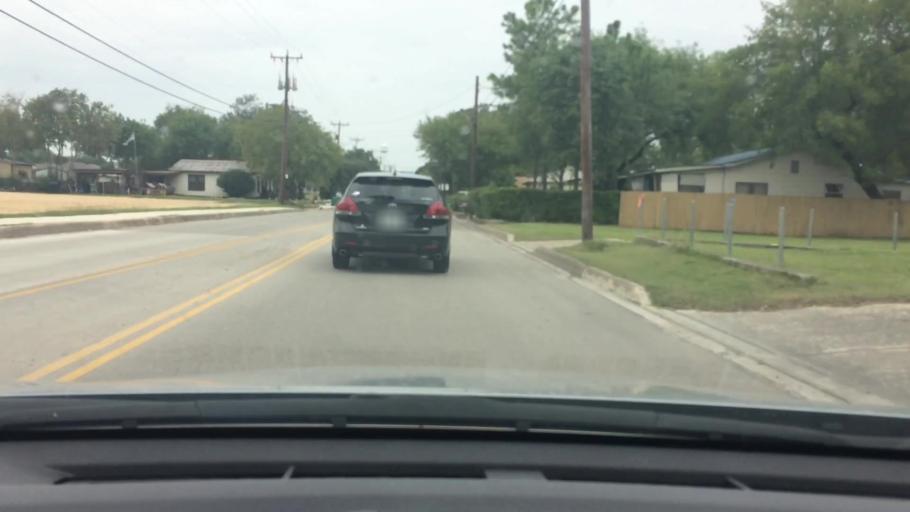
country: US
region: Texas
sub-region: Bexar County
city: Converse
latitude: 29.5191
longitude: -98.3167
